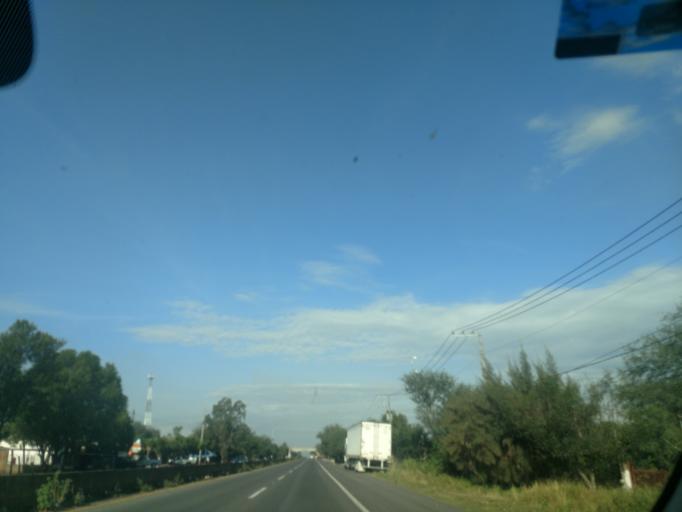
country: MX
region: Jalisco
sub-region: Ameca
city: Los Pocitos
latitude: 20.5374
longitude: -103.9332
